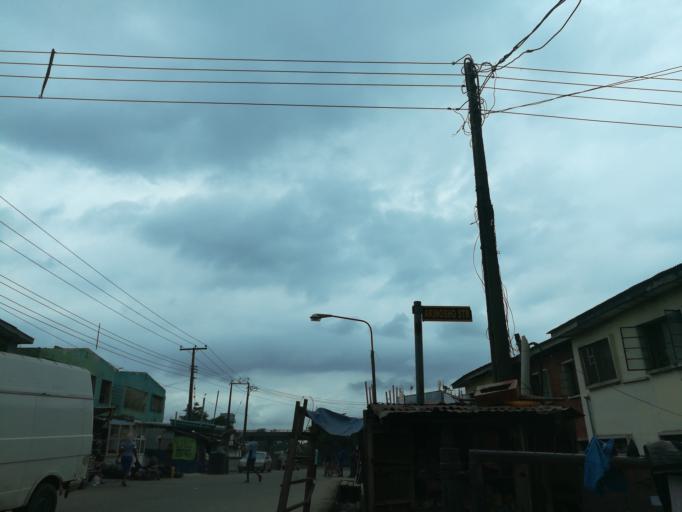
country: NG
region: Lagos
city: Oshodi
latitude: 6.5502
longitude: 3.3380
